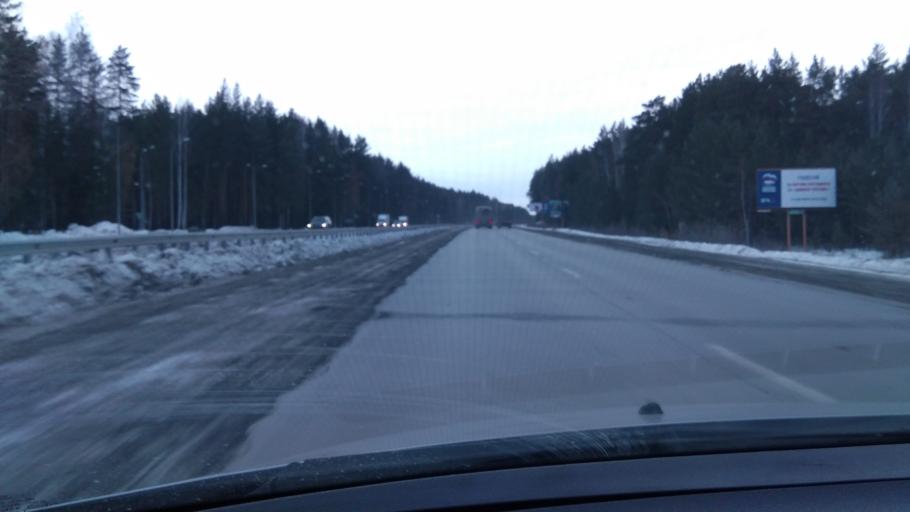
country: RU
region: Sverdlovsk
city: Sysert'
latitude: 56.5699
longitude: 60.8623
